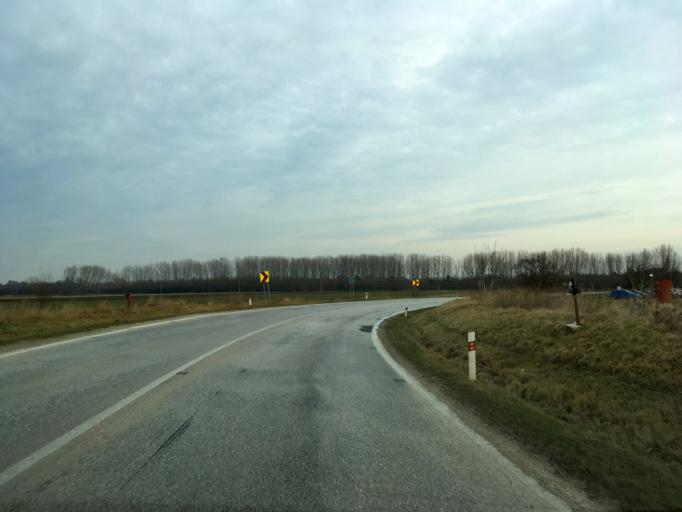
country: SK
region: Nitriansky
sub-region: Okres Nove Zamky
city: Nove Zamky
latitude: 47.9981
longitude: 18.2529
